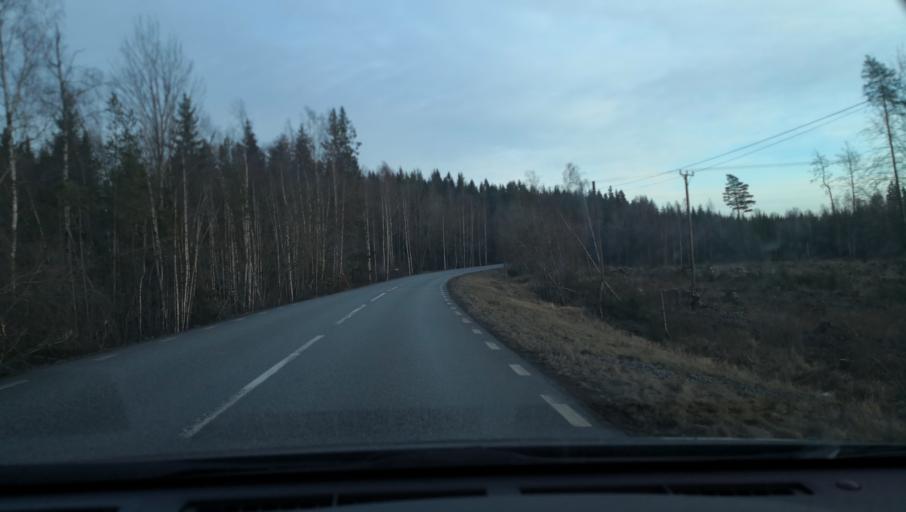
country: SE
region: OErebro
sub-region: Degerfors Kommun
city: Degerfors
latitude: 59.1386
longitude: 14.4561
